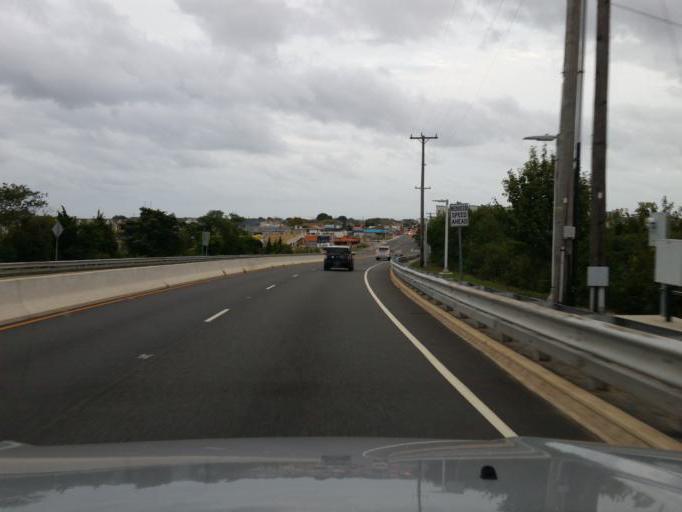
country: US
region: New Jersey
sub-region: Cape May County
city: Wildwood Crest
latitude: 38.9907
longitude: -74.8329
